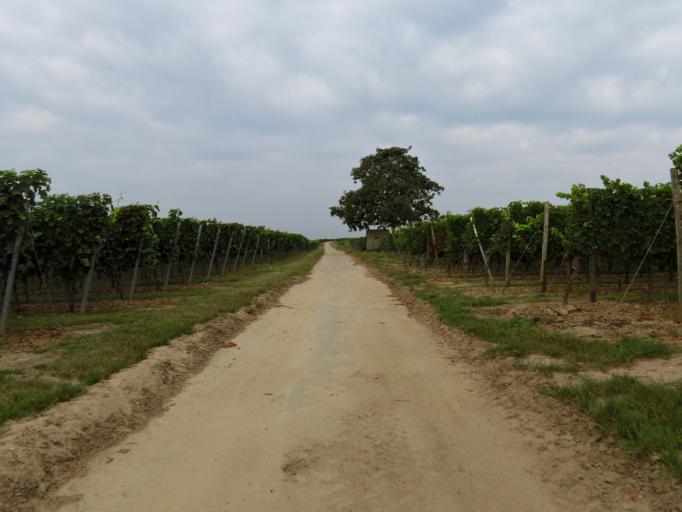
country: DE
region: Rheinland-Pfalz
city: Heuchelheim bei Frankenthal
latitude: 49.5740
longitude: 8.2829
